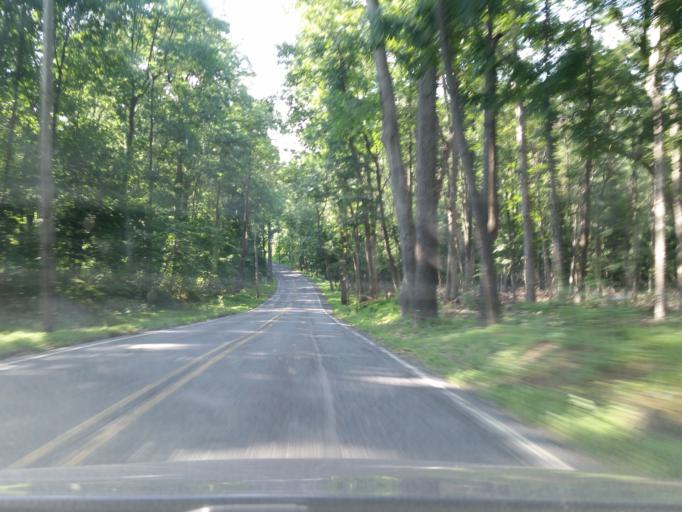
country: US
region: Pennsylvania
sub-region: Lebanon County
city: Campbelltown
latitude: 40.2320
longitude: -76.5057
